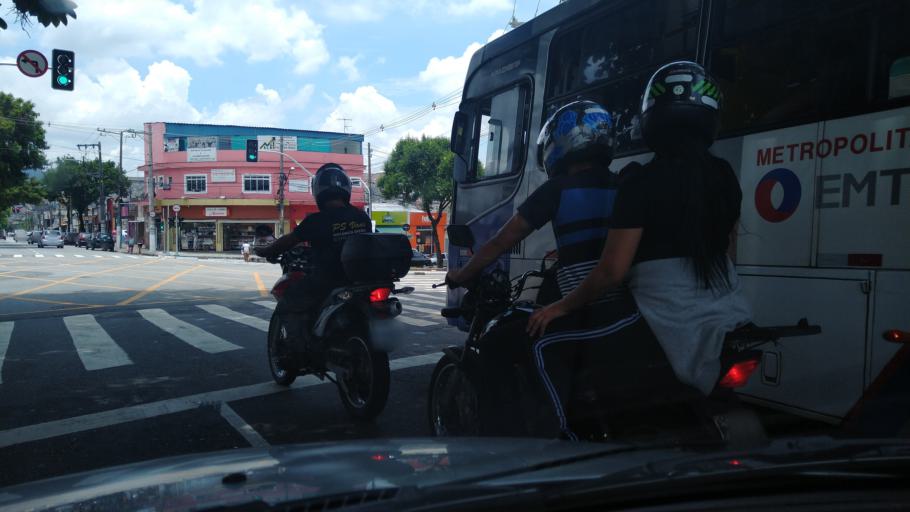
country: BR
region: Sao Paulo
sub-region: Osasco
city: Osasco
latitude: -23.5107
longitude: -46.7778
